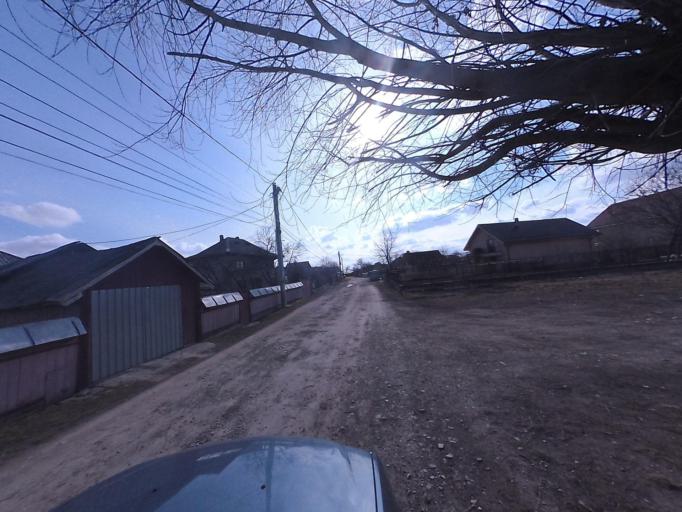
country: RO
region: Neamt
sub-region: Oras Targu Neamt
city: Targu Neamt
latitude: 47.2061
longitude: 26.3837
